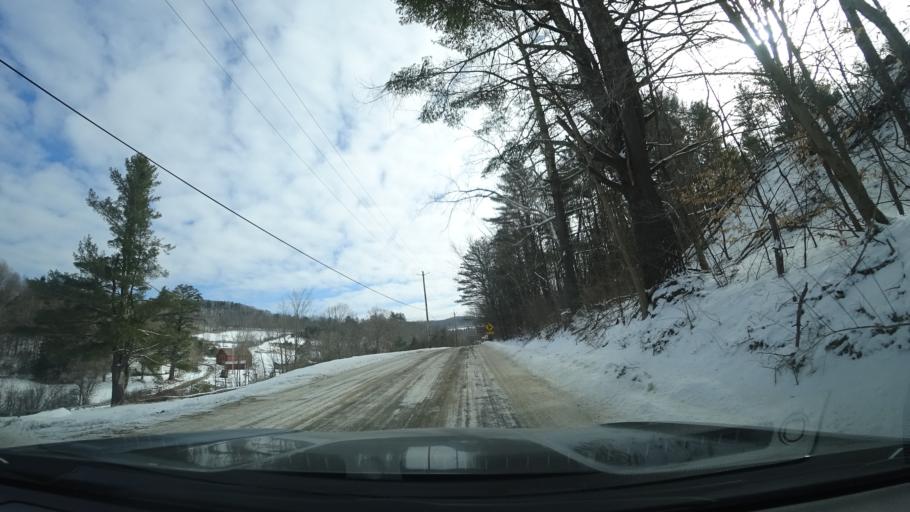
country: US
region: New York
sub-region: Washington County
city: Greenwich
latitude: 43.2283
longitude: -73.3694
